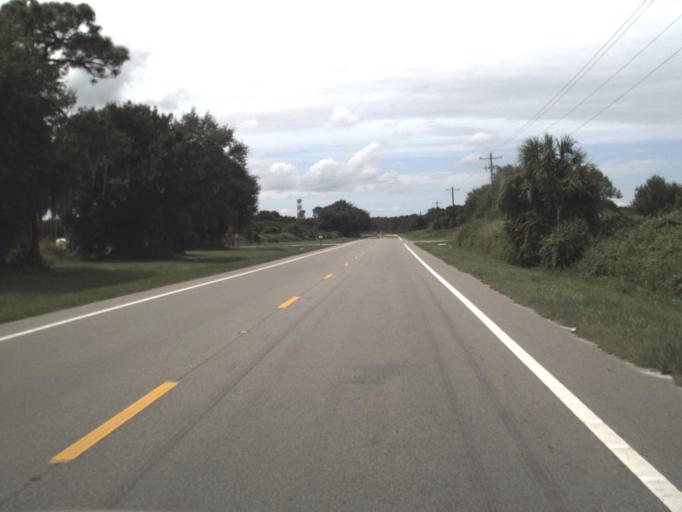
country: US
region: Florida
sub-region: Hillsborough County
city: Wimauma
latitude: 27.5995
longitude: -82.2914
